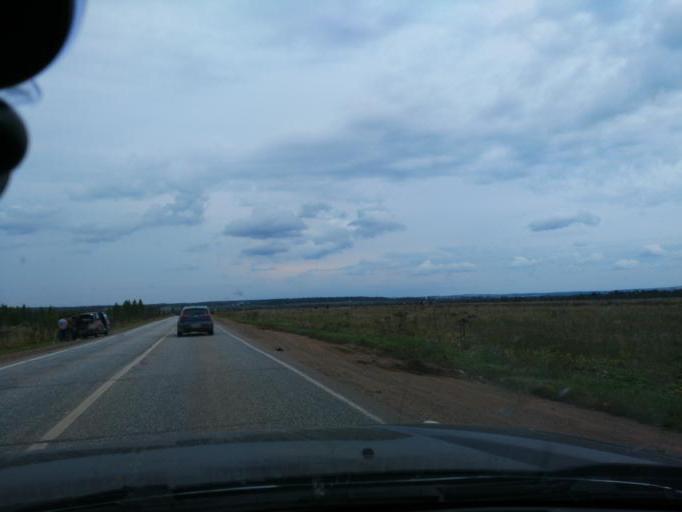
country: RU
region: Perm
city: Chernushka
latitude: 56.5048
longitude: 55.9902
